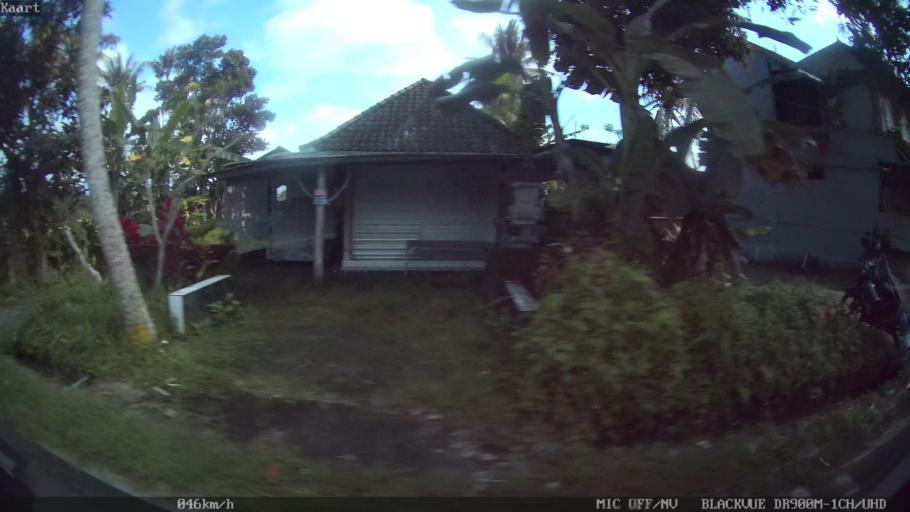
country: ID
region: Bali
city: Banjar Pesalakan
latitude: -8.4993
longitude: 115.2955
